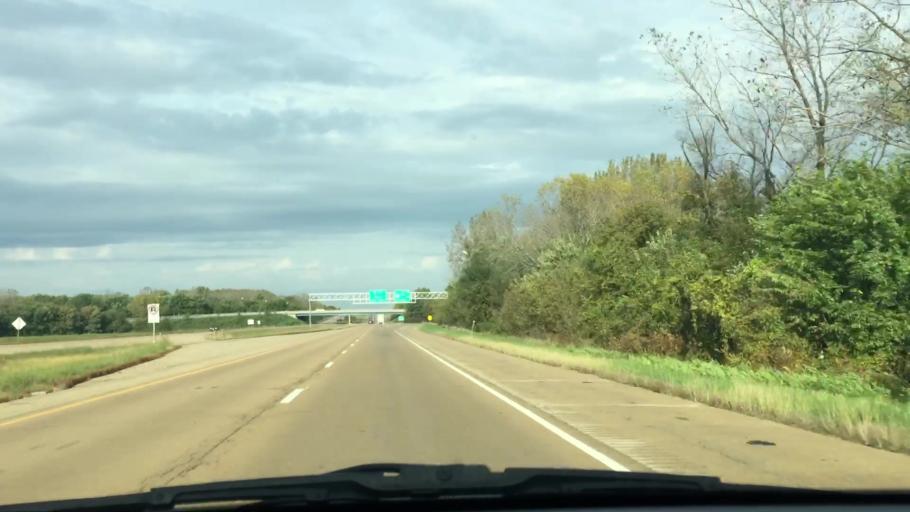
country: US
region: Illinois
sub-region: Whiteside County
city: Sterling
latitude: 41.7579
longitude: -89.7770
